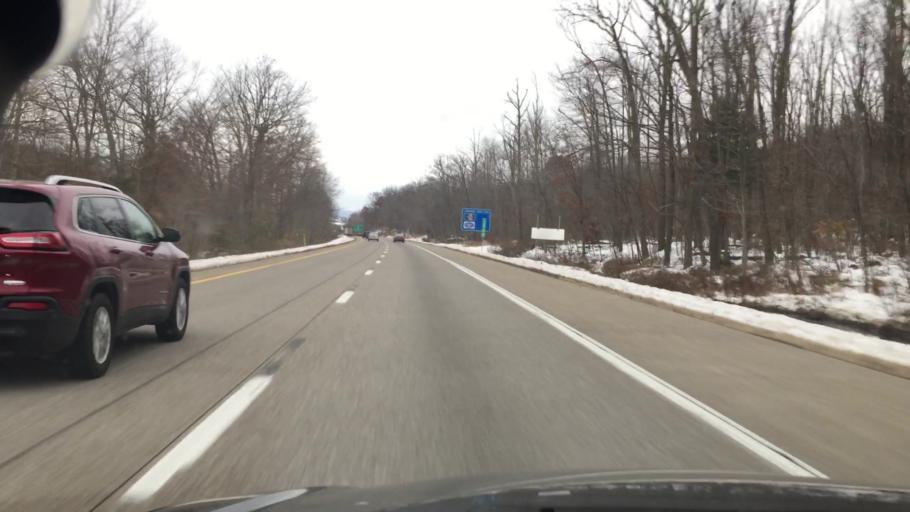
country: US
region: Pennsylvania
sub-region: Luzerne County
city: Conyngham
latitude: 41.0329
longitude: -76.0649
